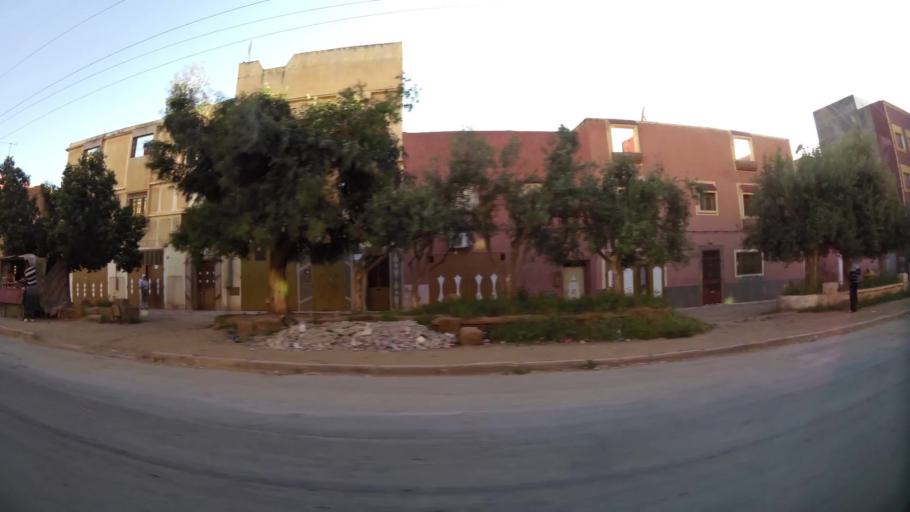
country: MA
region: Oriental
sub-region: Berkane-Taourirt
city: Berkane
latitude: 34.9246
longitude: -2.3130
